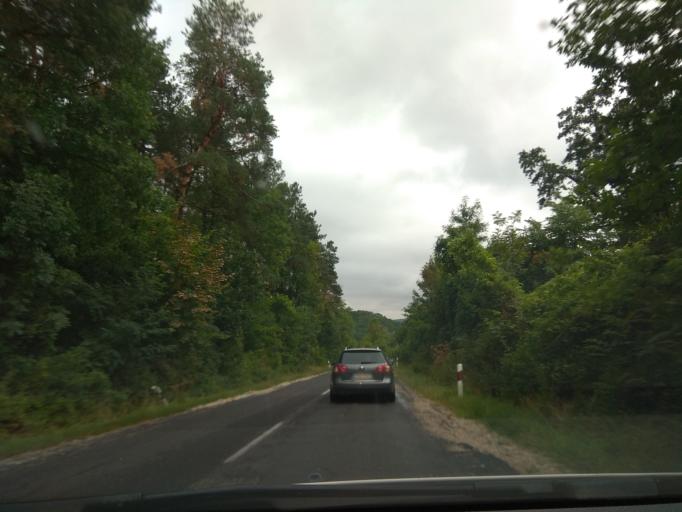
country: HU
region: Borsod-Abauj-Zemplen
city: Harsany
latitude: 48.0174
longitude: 20.7643
